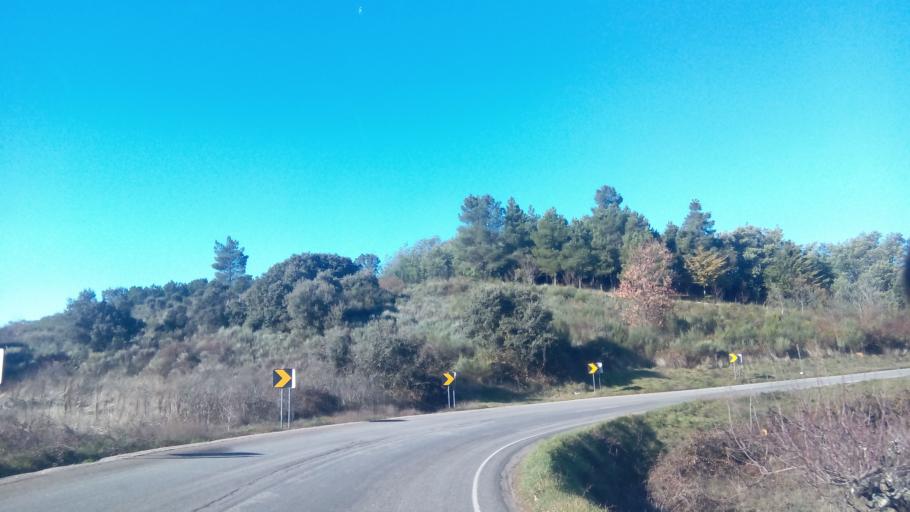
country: PT
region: Braganca
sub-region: Vimioso
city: Vimioso
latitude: 41.6595
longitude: -6.6101
